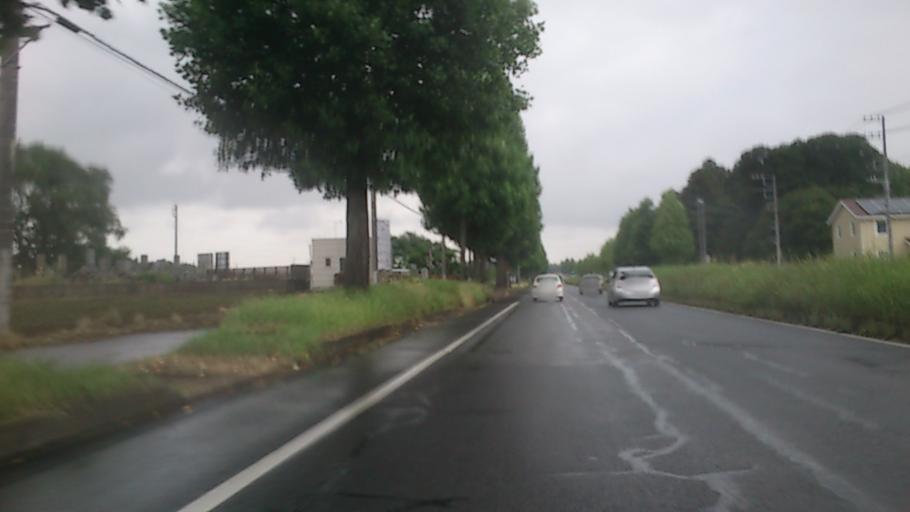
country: JP
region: Ibaraki
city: Naka
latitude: 36.0125
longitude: 140.1462
